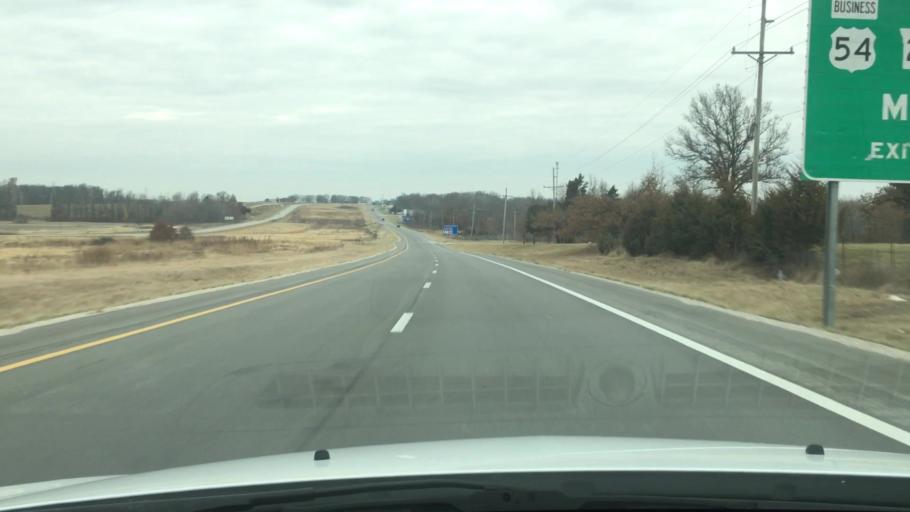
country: US
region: Missouri
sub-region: Audrain County
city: Mexico
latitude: 39.1011
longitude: -91.8966
